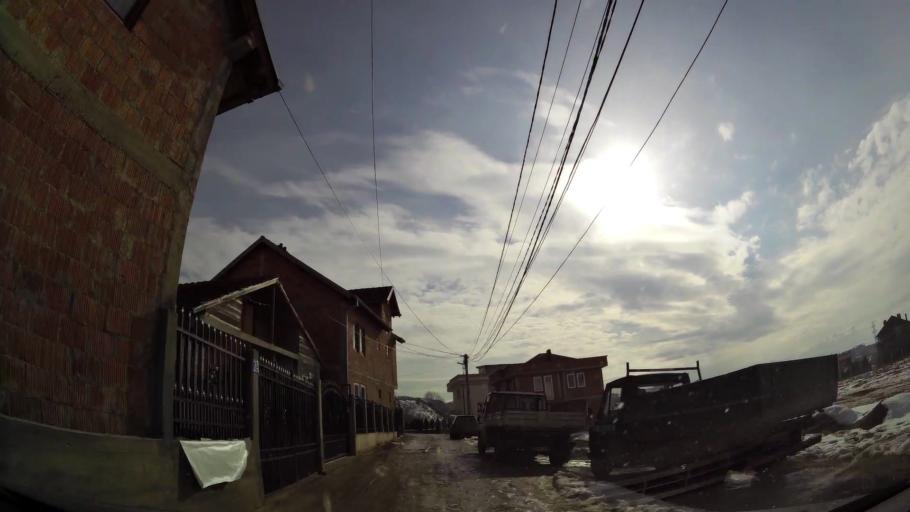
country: XK
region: Pristina
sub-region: Komuna e Prishtines
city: Pristina
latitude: 42.6893
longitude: 21.1563
